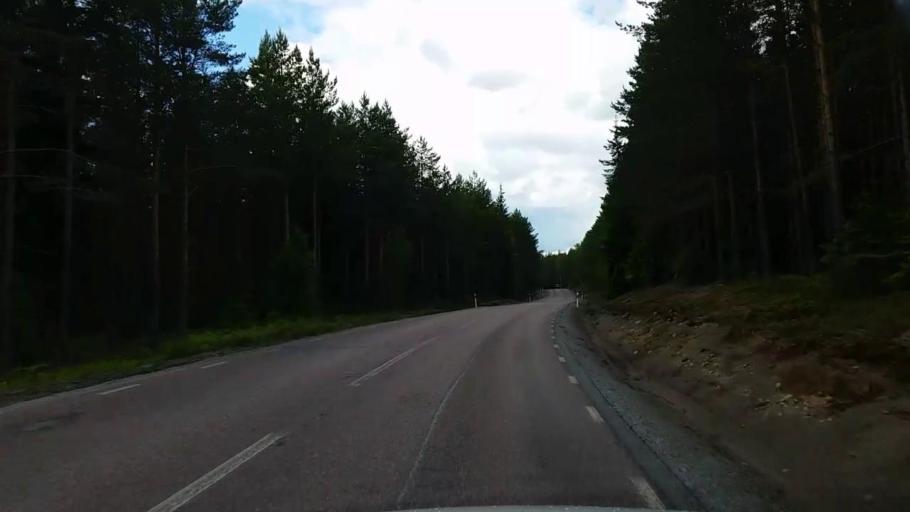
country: SE
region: Vaestmanland
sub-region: Fagersta Kommun
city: Fagersta
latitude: 59.9013
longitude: 15.8200
